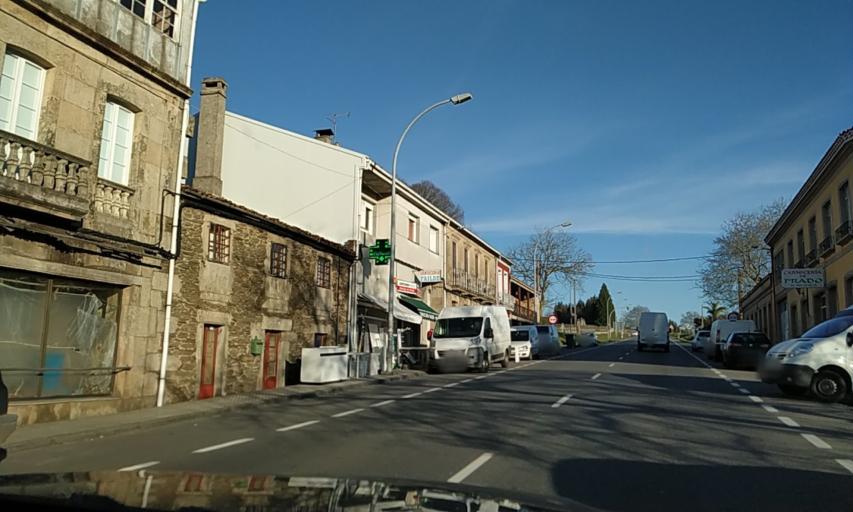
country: ES
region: Galicia
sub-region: Provincia de Pontevedra
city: Silleda
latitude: 42.6824
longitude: -8.1810
